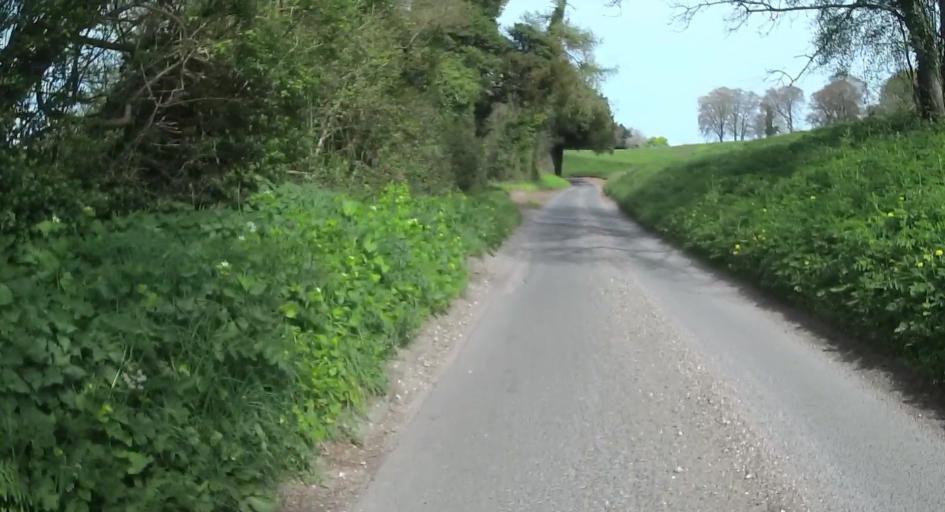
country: GB
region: England
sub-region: Hampshire
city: Chandlers Ford
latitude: 51.0710
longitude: -1.4502
